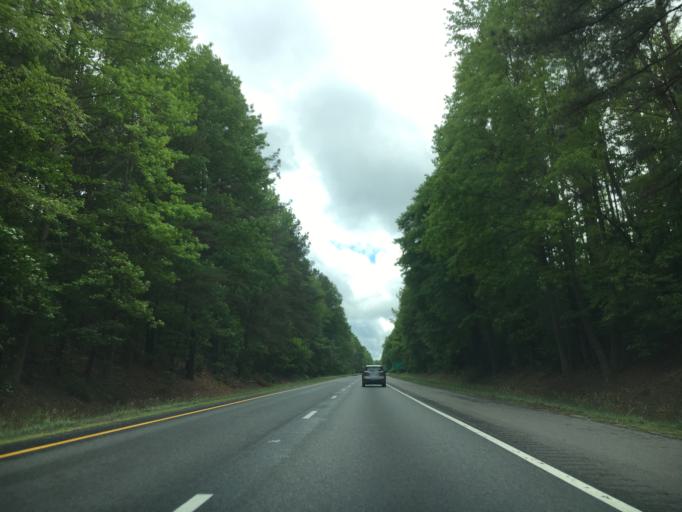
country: US
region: Virginia
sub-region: Mecklenburg County
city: South Hill
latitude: 36.7339
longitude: -78.1032
